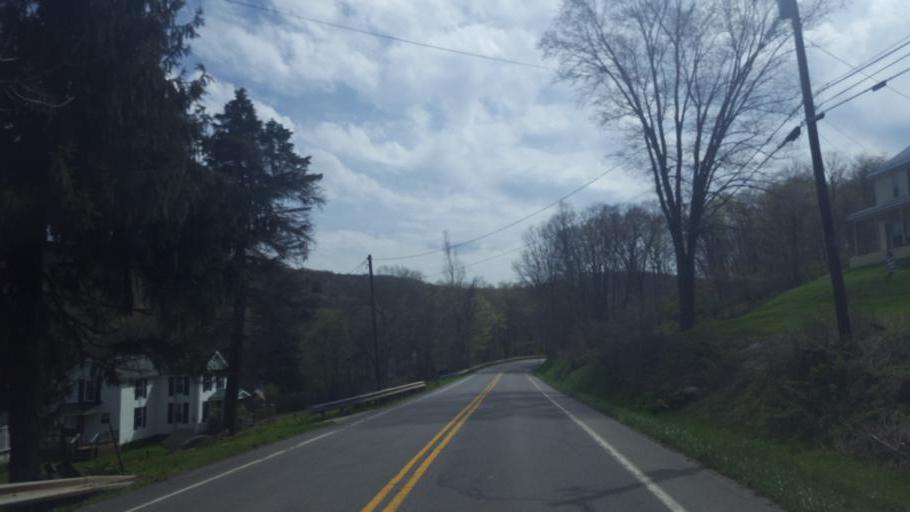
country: US
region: Pennsylvania
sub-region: Venango County
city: Sugarcreek
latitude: 41.3572
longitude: -79.9373
